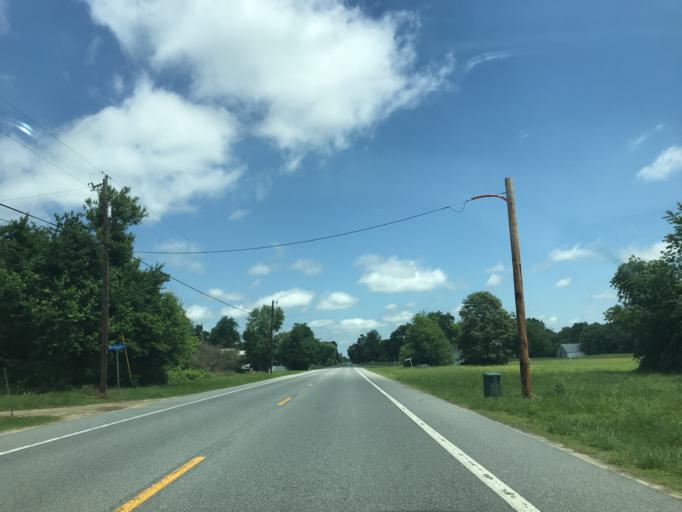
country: US
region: Maryland
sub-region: Caroline County
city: Federalsburg
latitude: 38.7077
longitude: -75.7495
